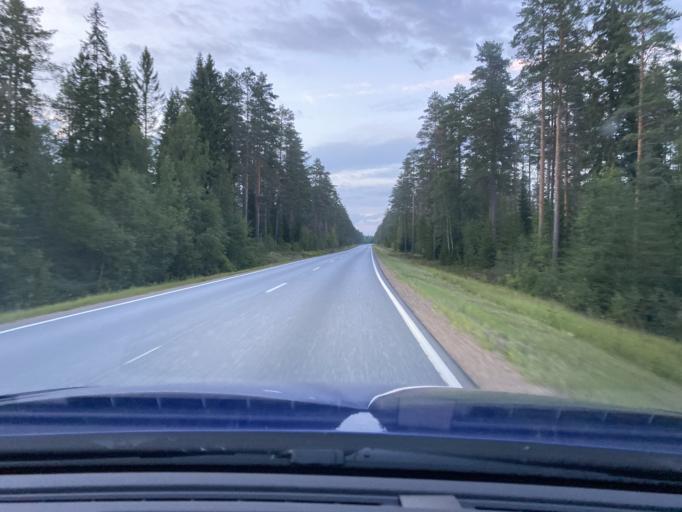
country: FI
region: Satakunta
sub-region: Pohjois-Satakunta
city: Honkajoki
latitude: 62.1360
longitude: 22.2514
